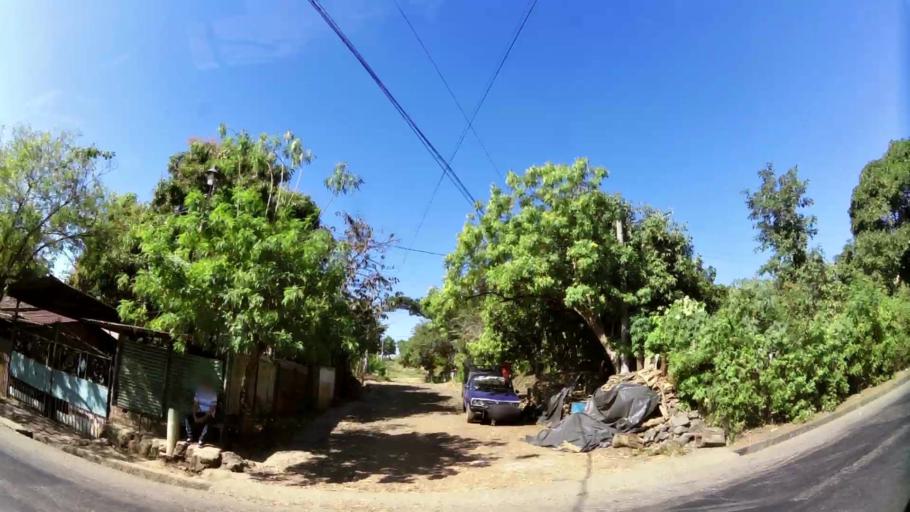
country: SV
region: Sonsonate
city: Sonzacate
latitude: 13.7376
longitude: -89.7341
